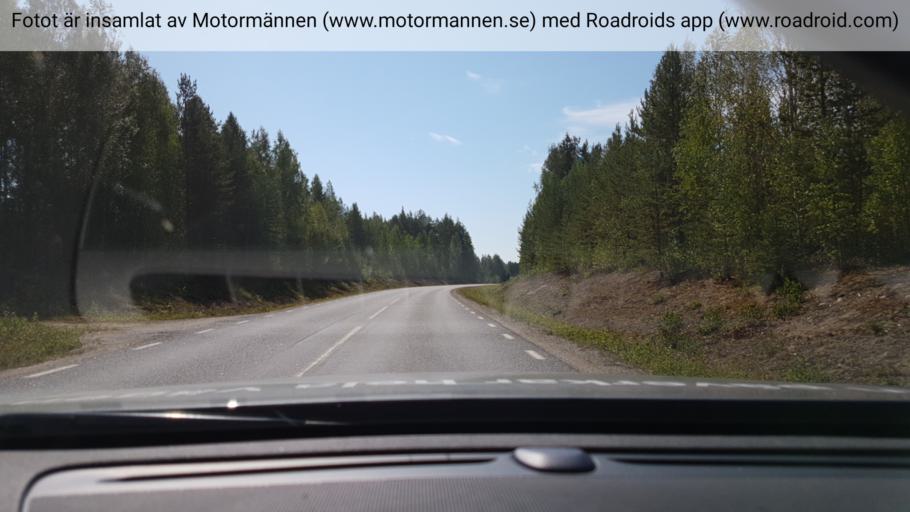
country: SE
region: Vaesterbotten
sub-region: Vindelns Kommun
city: Vindeln
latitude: 64.2907
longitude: 19.6206
